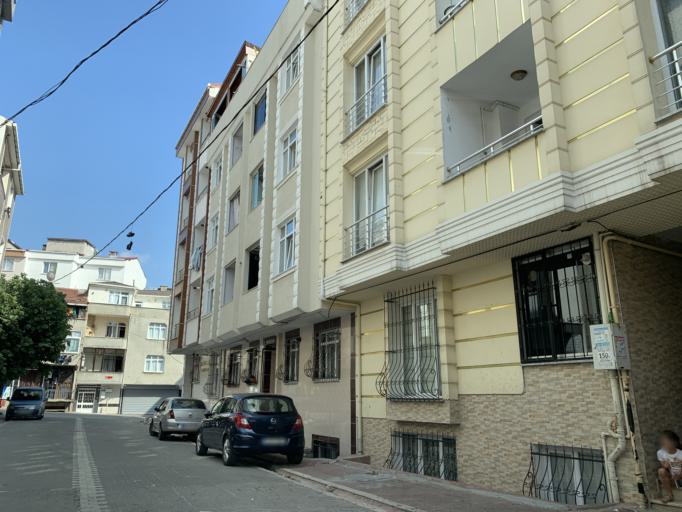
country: TR
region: Istanbul
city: Esenyurt
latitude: 41.0341
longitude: 28.6723
